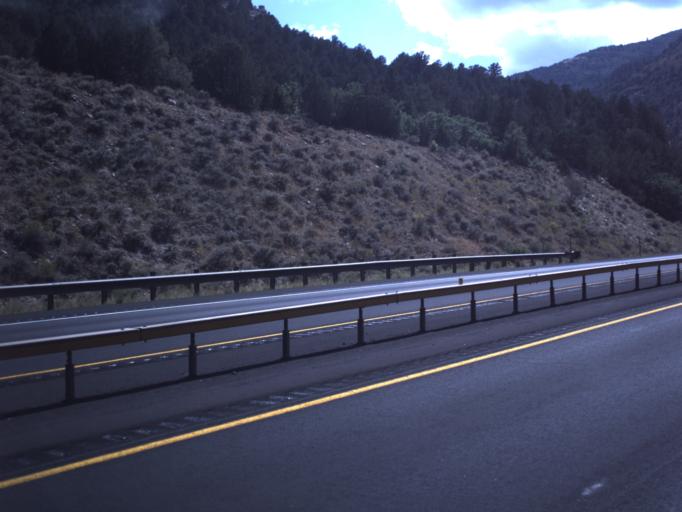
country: US
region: Utah
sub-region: Sevier County
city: Salina
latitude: 38.9015
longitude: -111.6330
